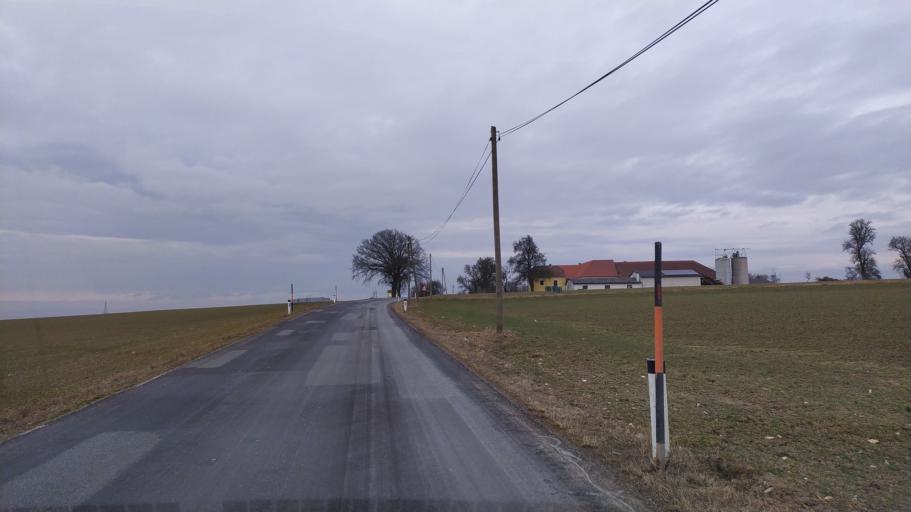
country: AT
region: Lower Austria
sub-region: Politischer Bezirk Amstetten
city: Zeillern
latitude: 48.1242
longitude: 14.7447
